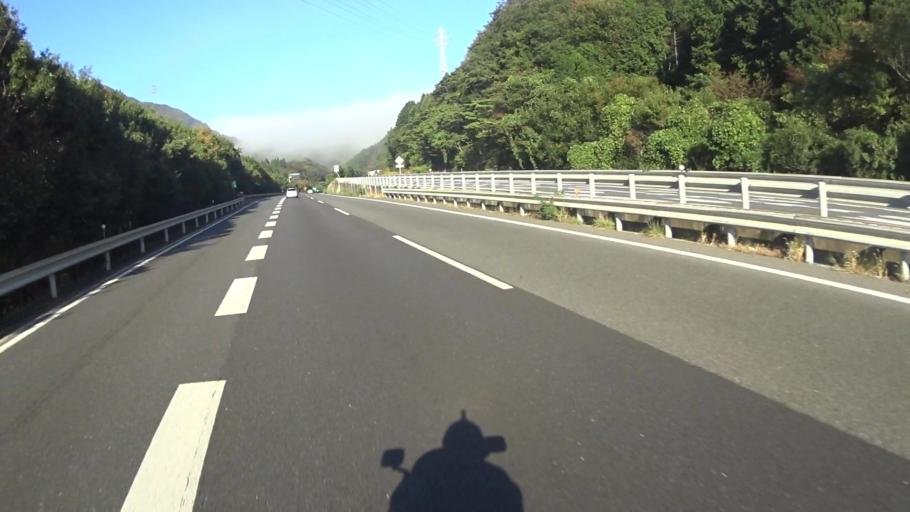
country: JP
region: Kyoto
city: Muko
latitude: 34.9841
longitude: 135.6501
